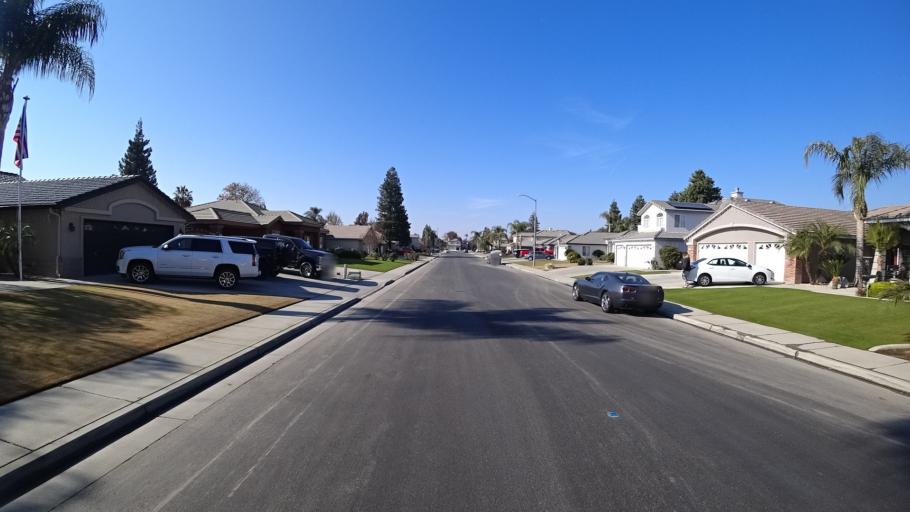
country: US
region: California
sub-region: Kern County
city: Greenacres
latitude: 35.3163
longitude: -119.1230
